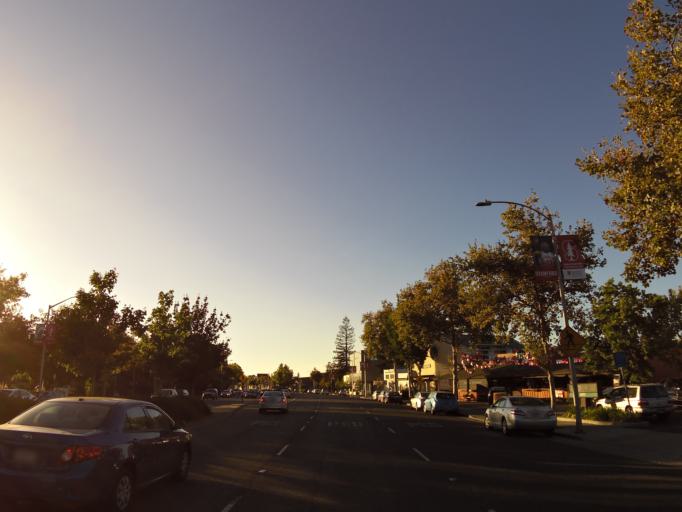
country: US
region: California
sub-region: Santa Clara County
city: Los Altos
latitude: 37.4139
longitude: -122.1260
